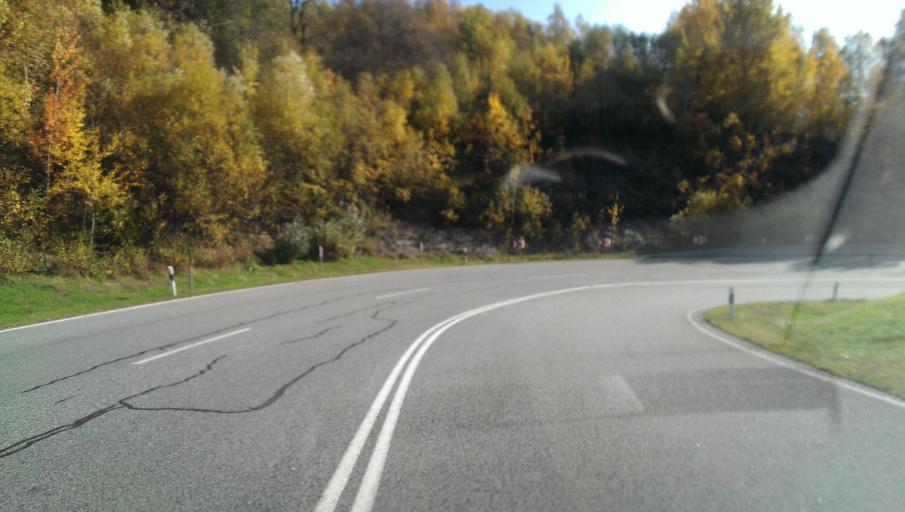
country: DE
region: Saxony
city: Barenstein
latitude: 50.7813
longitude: 13.8337
